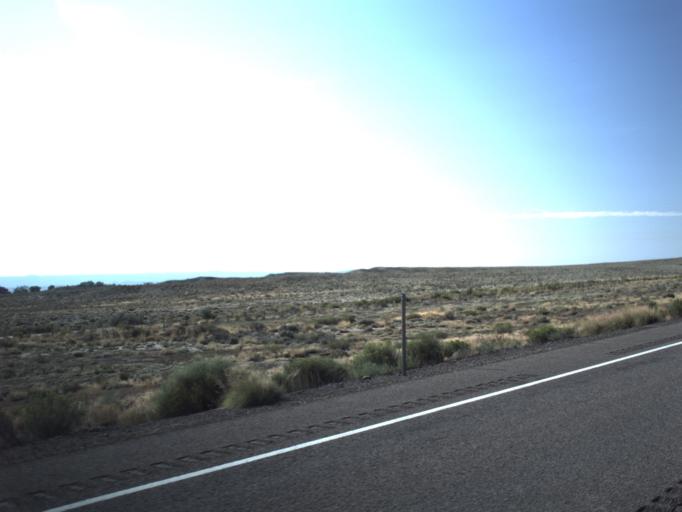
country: US
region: Utah
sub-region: Emery County
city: Huntington
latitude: 39.4271
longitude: -110.8694
